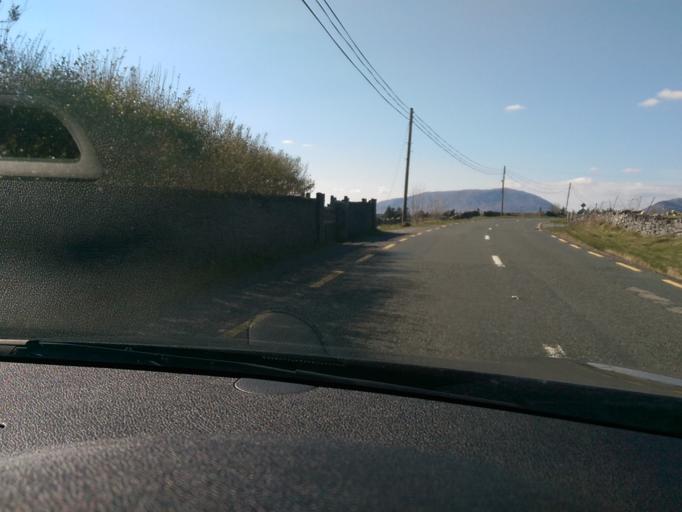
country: IE
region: Connaught
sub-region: County Galway
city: Oughterard
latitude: 53.4369
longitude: -9.4422
